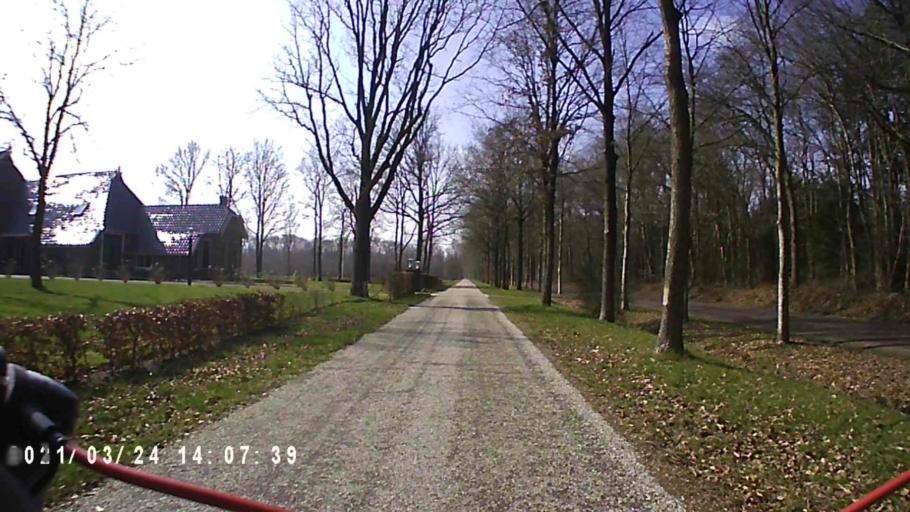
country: NL
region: Friesland
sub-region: Gemeente Smallingerland
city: Drachtstercompagnie
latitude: 53.0751
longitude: 6.2438
